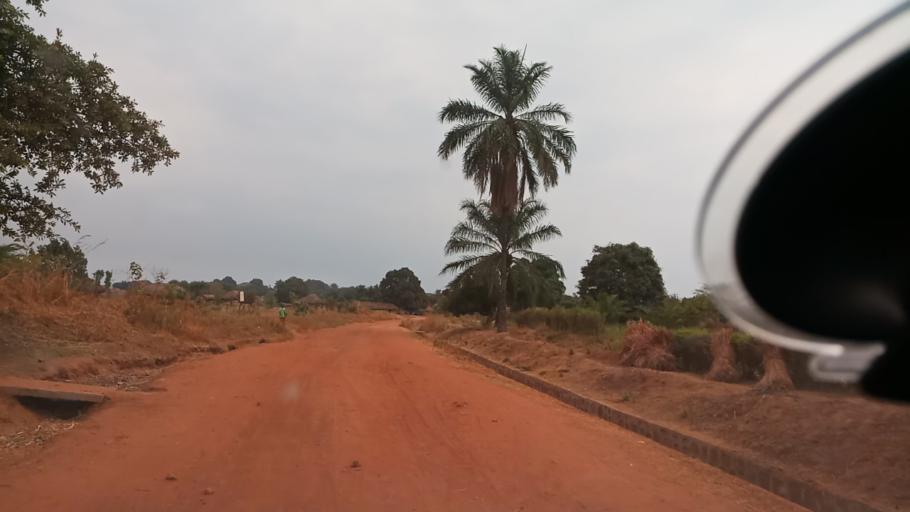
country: ZM
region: Luapula
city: Nchelenge
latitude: -9.1054
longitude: 28.3012
